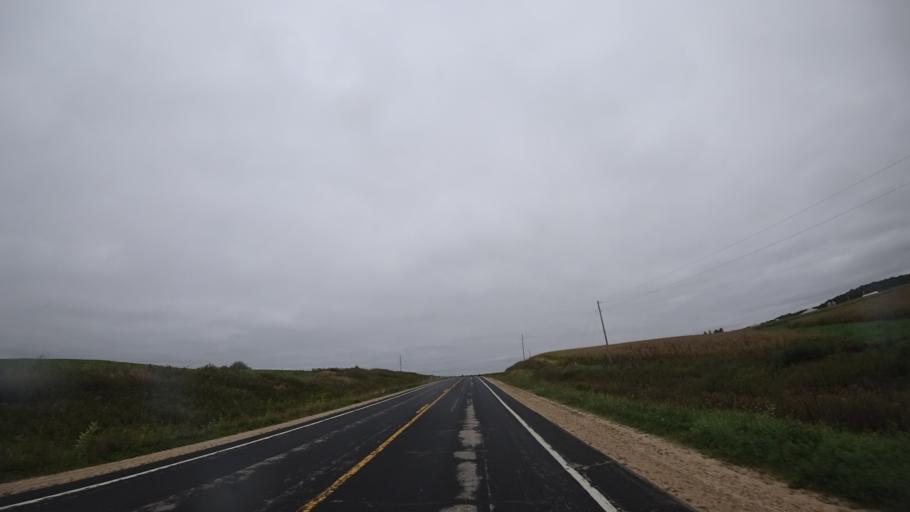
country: US
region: Wisconsin
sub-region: Grant County
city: Boscobel
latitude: 43.1072
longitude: -90.8088
